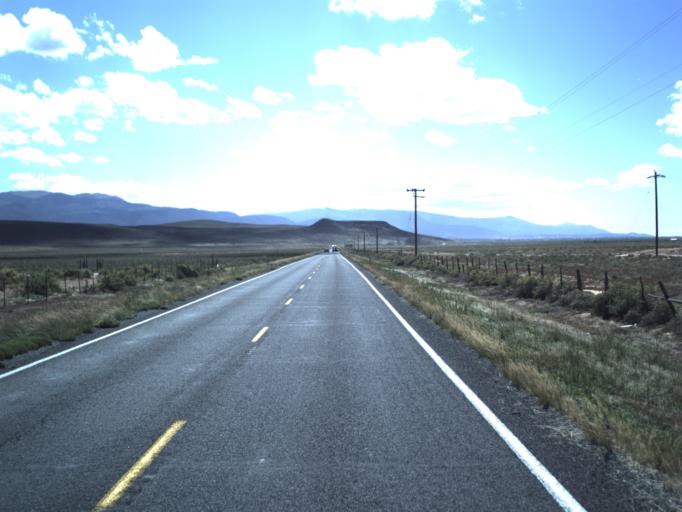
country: US
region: Utah
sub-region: Iron County
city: Enoch
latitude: 37.8762
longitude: -113.0316
